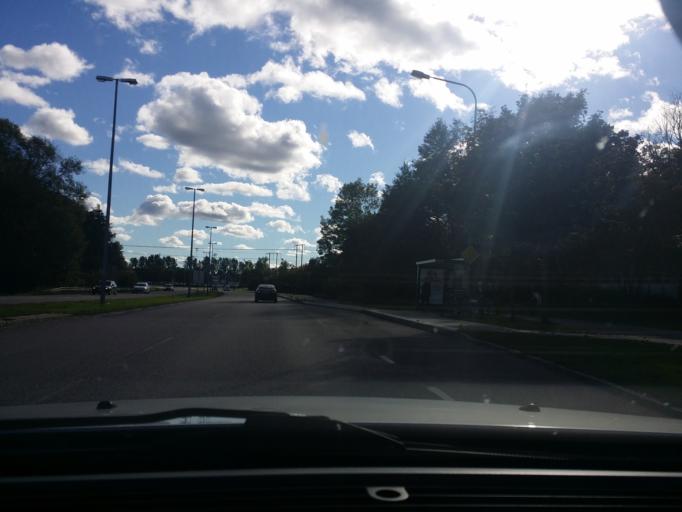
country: SE
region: Vaestmanland
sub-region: Vasteras
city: Vasteras
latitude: 59.6352
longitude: 16.5319
